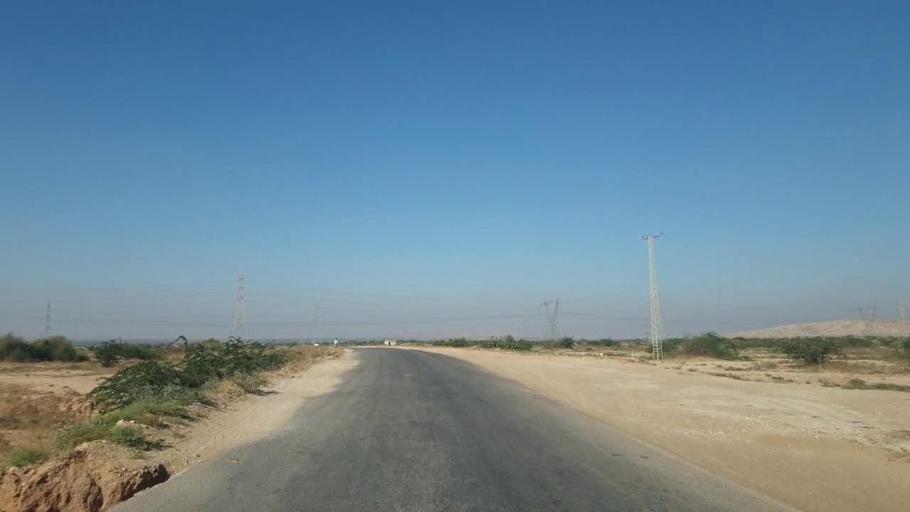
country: PK
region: Sindh
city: Gharo
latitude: 25.1717
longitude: 67.6601
